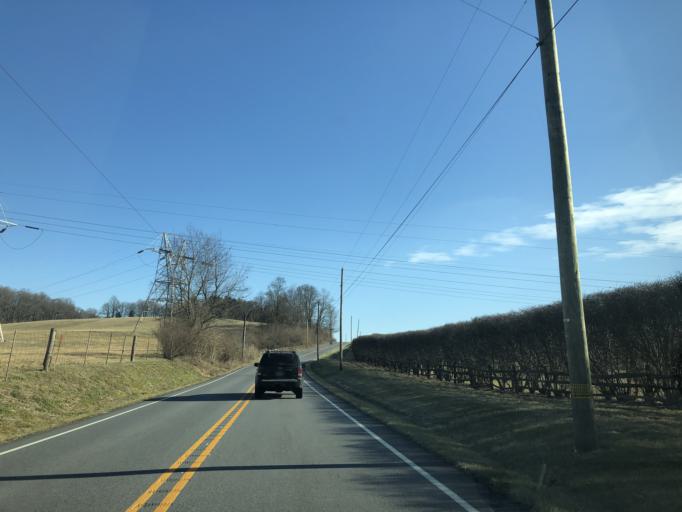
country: US
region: Pennsylvania
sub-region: Chester County
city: Upland
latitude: 39.9072
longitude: -75.7993
